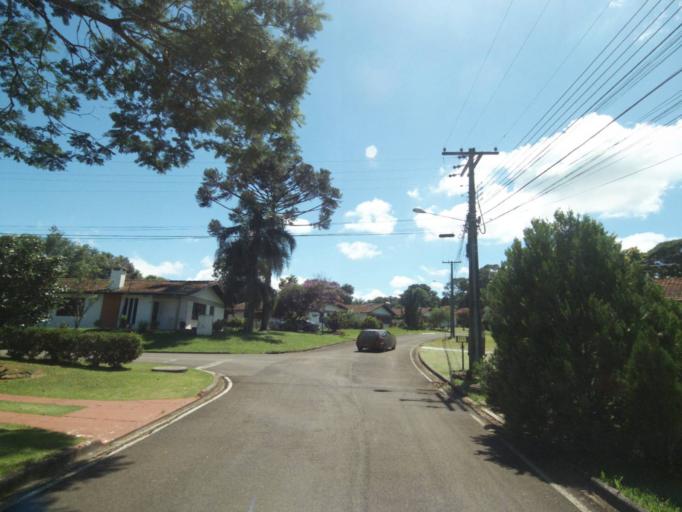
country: BR
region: Parana
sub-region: Chopinzinho
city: Chopinzinho
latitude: -25.7985
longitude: -52.0955
